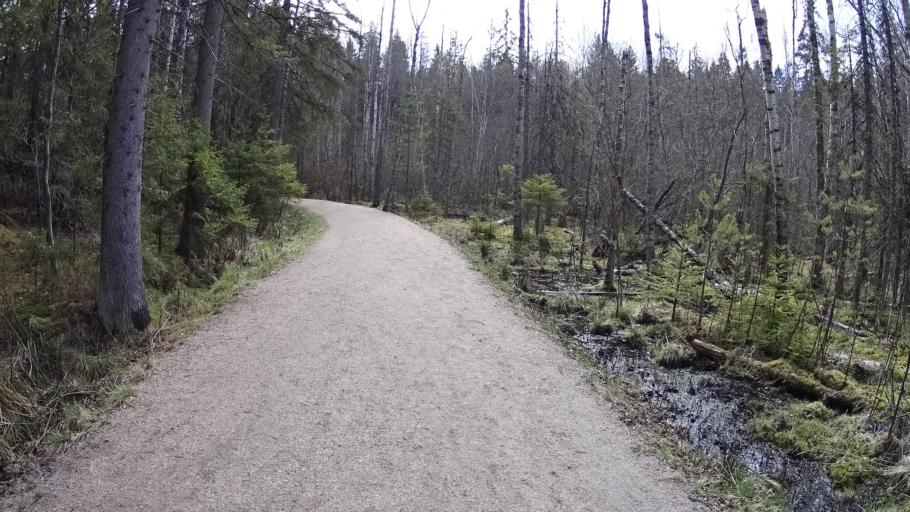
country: FI
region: Uusimaa
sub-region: Helsinki
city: Espoo
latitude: 60.2646
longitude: 24.6374
